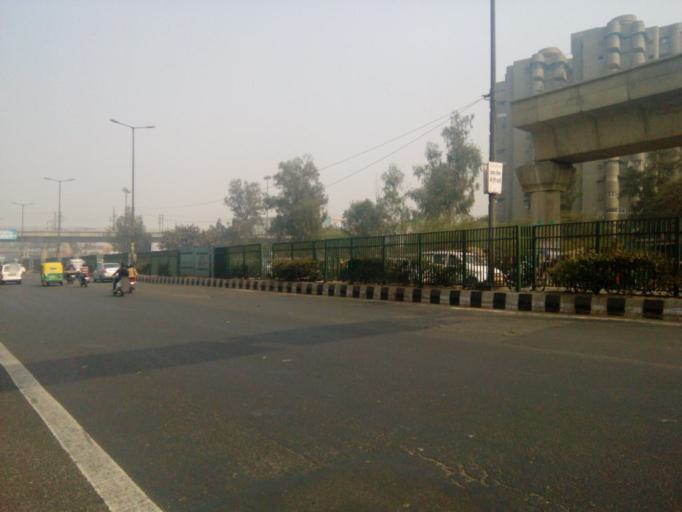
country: IN
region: Uttar Pradesh
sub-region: Gautam Buddha Nagar
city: Noida
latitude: 28.6443
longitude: 77.3166
